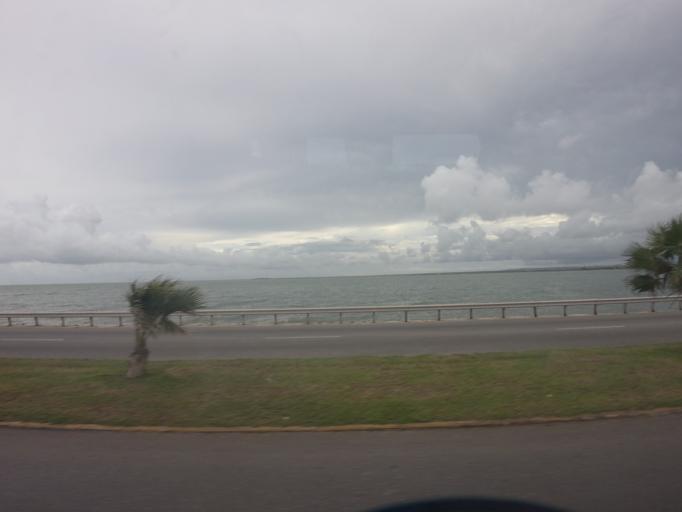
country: CU
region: Matanzas
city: Varadero
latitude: 23.1446
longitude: -81.2639
